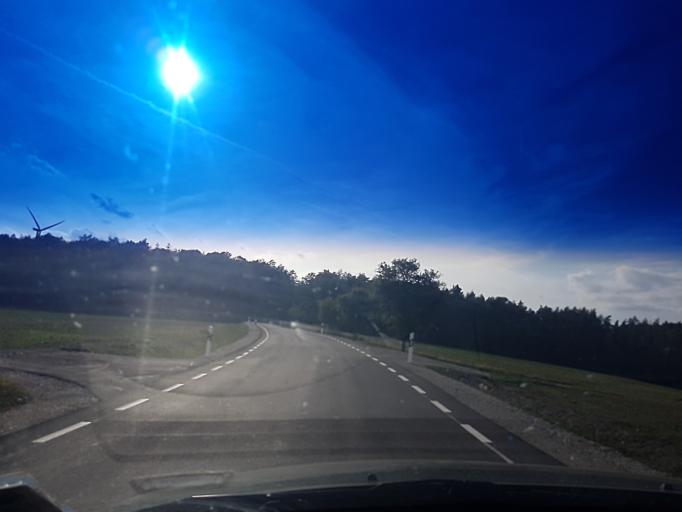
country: DE
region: Bavaria
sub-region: Upper Franconia
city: Burgwindheim
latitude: 49.7919
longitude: 10.5784
